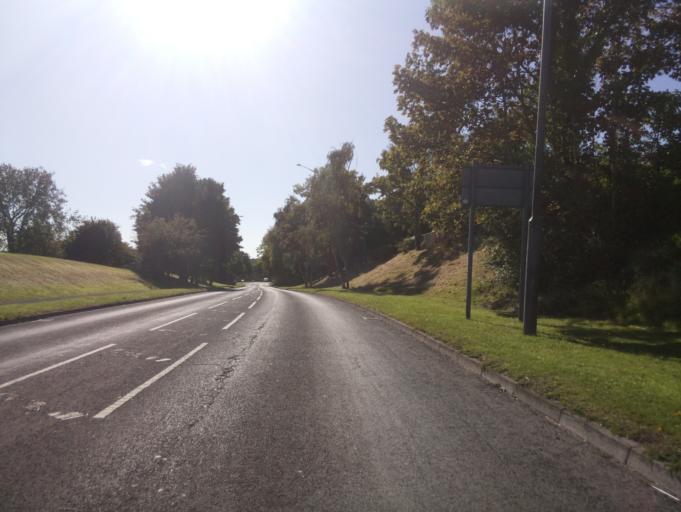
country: GB
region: Wales
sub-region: Torfaen County Borough
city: Cwmbran
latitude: 51.6538
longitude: -3.0470
